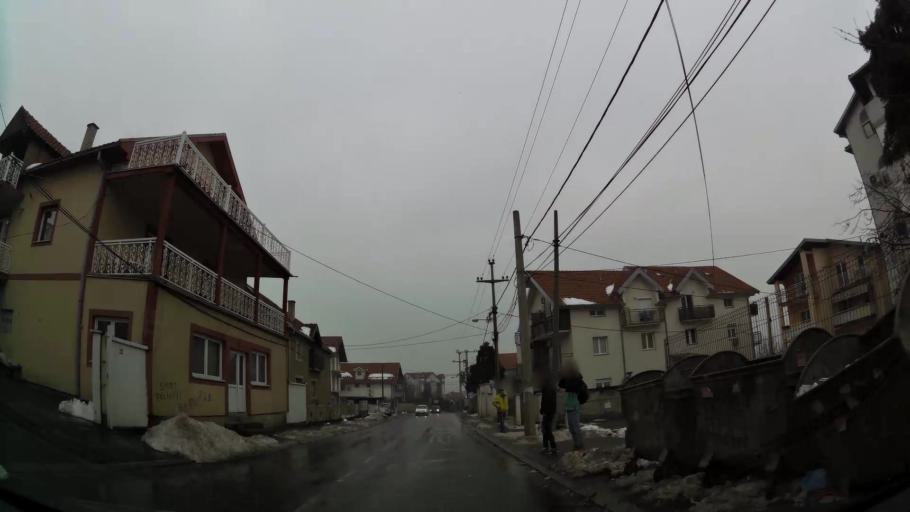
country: RS
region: Central Serbia
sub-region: Belgrade
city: Zvezdara
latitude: 44.7680
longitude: 20.5134
